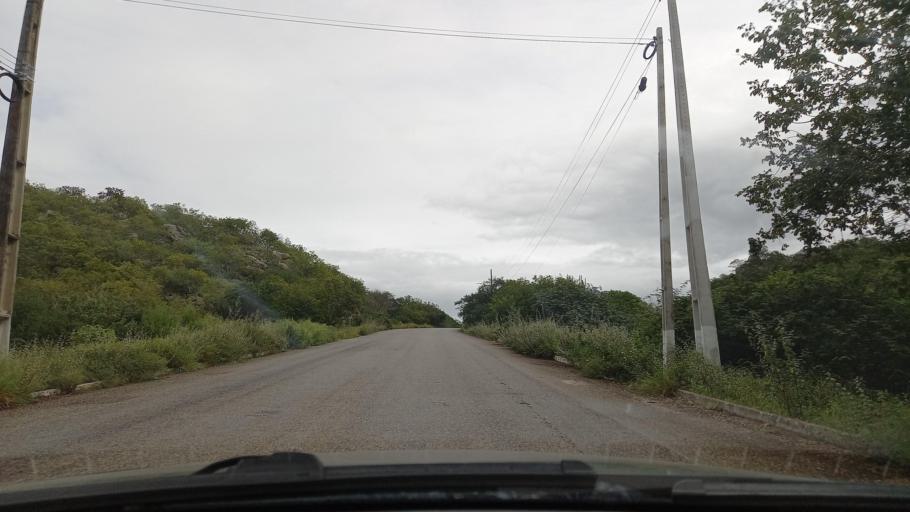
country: BR
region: Sergipe
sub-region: Caninde De Sao Francisco
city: Caninde de Sao Francisco
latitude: -9.6324
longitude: -37.7798
